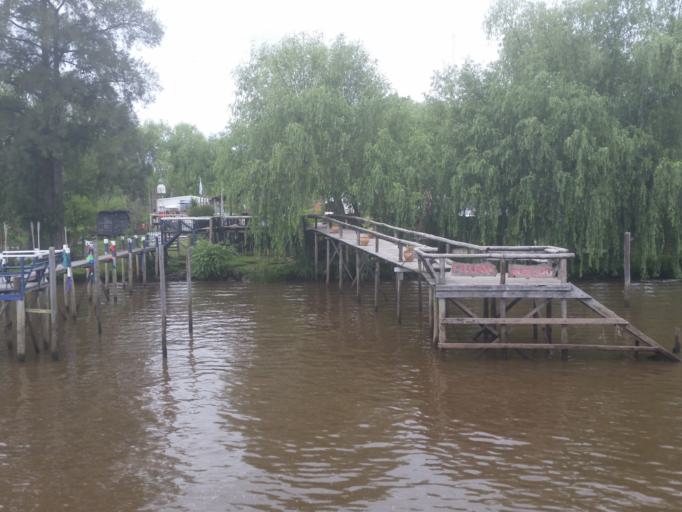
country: AR
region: Buenos Aires
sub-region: Partido de Tigre
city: Tigre
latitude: -34.3983
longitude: -58.5730
